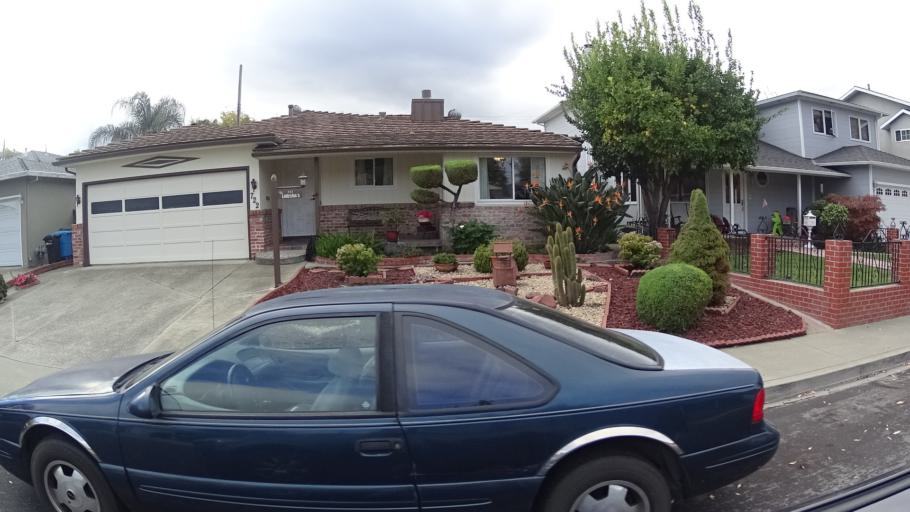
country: US
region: California
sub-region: Santa Clara County
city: Santa Clara
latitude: 37.3366
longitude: -121.9745
